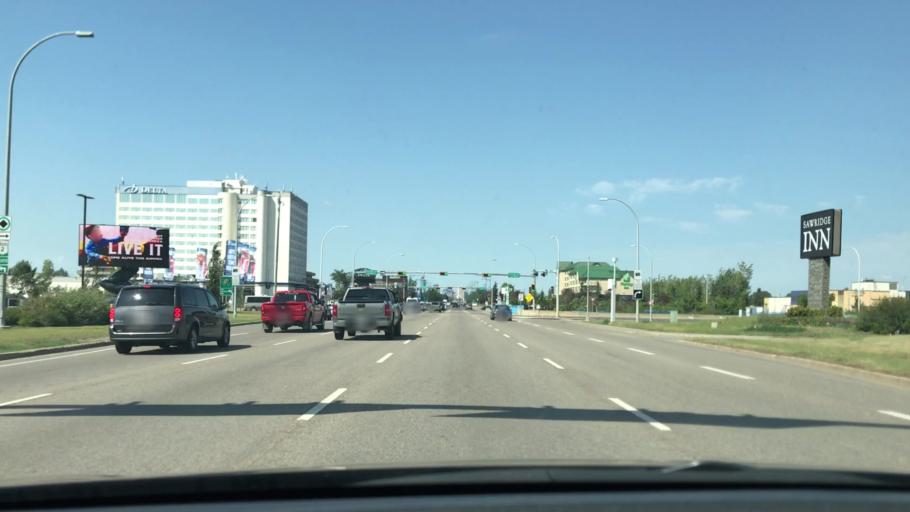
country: CA
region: Alberta
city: Edmonton
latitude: 53.4789
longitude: -113.4920
